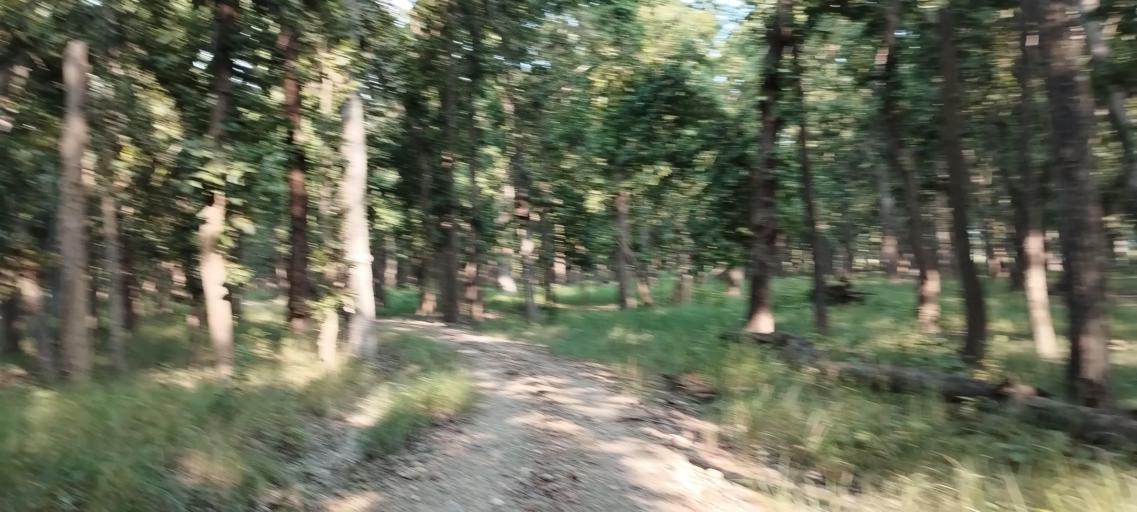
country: NP
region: Far Western
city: Tikapur
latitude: 28.5189
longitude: 81.2796
